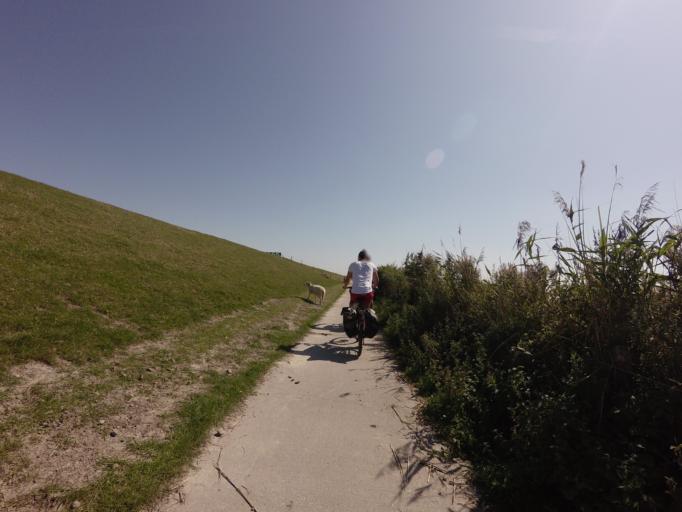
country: NL
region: Friesland
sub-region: Gemeente Dongeradeel
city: Anjum
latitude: 53.3989
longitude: 6.1011
